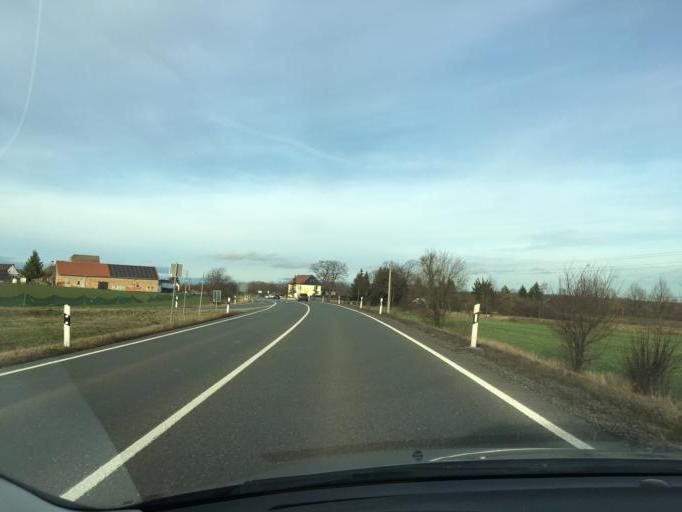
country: DE
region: Thuringia
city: Gerstenberg
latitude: 51.0243
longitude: 12.4573
